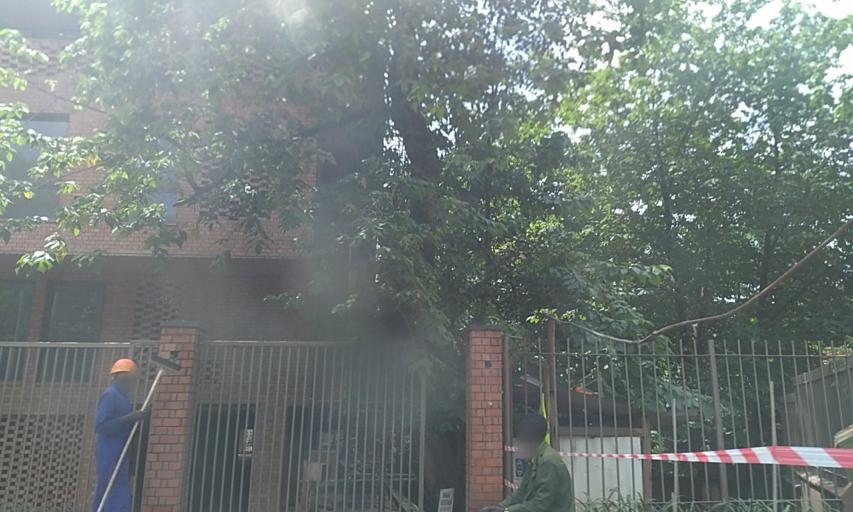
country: UG
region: Central Region
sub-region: Kampala District
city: Kampala
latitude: 0.3284
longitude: 32.6009
